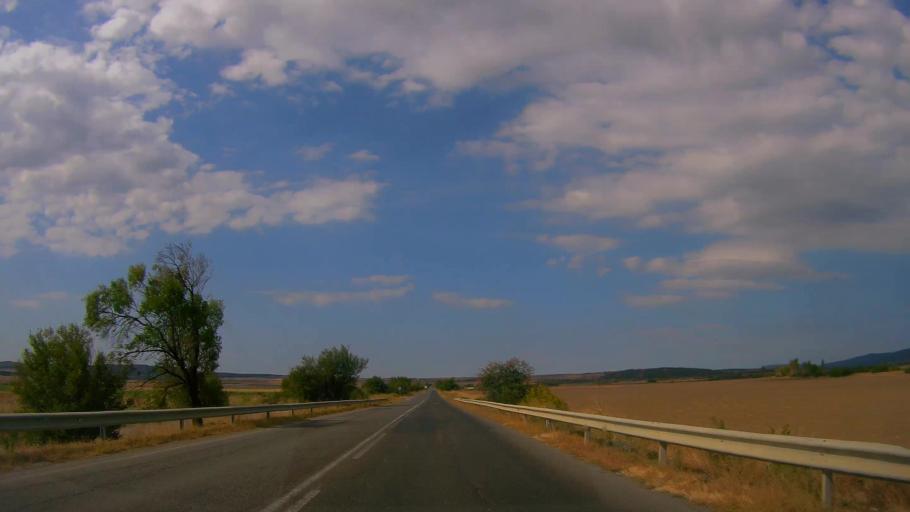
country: BG
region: Burgas
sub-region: Obshtina Aytos
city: Aytos
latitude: 42.7032
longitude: 27.2245
